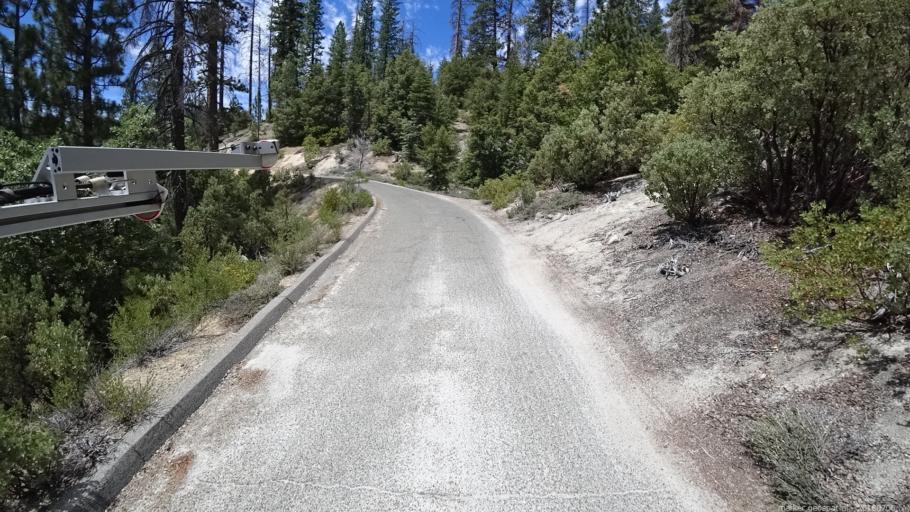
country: US
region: California
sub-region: Madera County
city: Oakhurst
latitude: 37.4131
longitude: -119.4025
